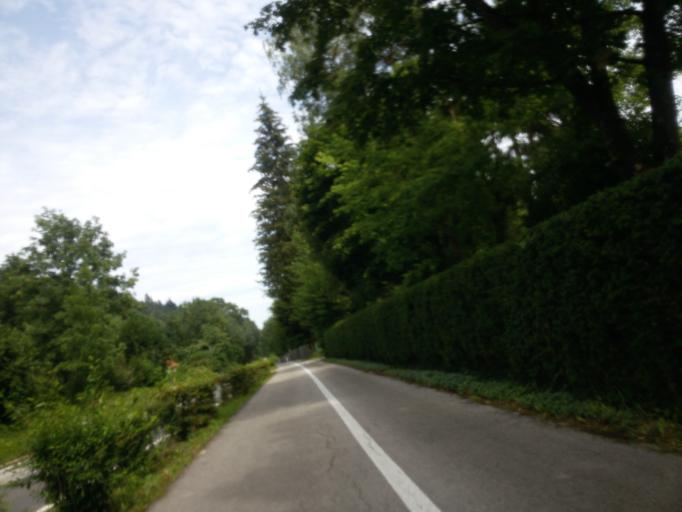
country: AT
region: Carinthia
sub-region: Politischer Bezirk Villach Land
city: Velden am Woerthersee
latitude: 46.6218
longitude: 14.0681
